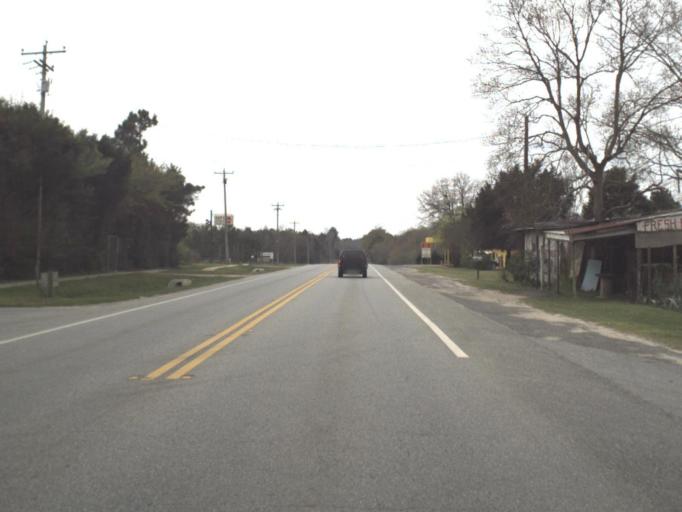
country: US
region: Florida
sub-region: Jackson County
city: Graceville
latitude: 30.9803
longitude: -85.6464
